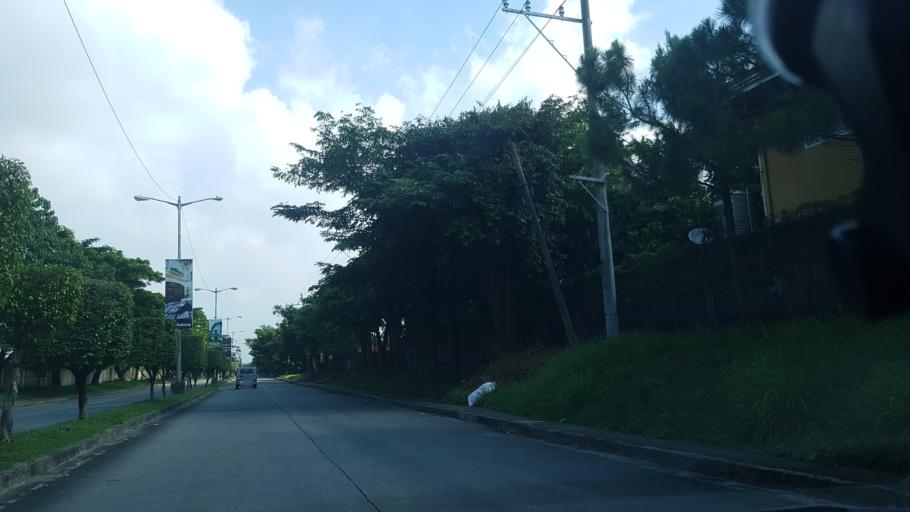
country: PH
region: Calabarzon
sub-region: Province of Laguna
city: Magsaysay
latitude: 14.3645
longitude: 121.0098
